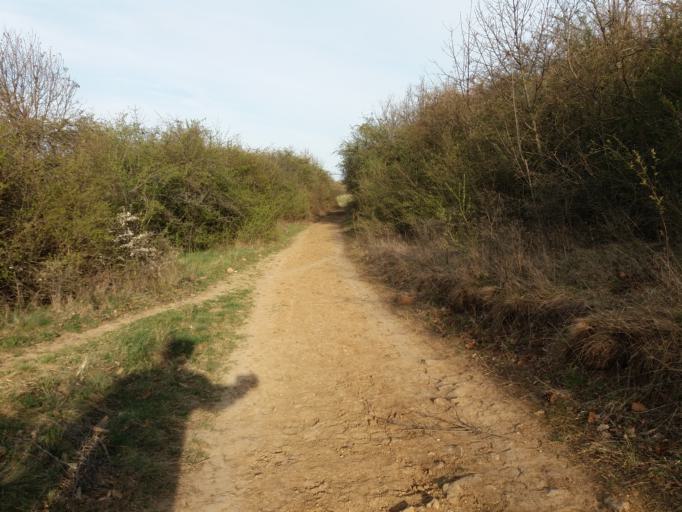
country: HU
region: Pest
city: Pilisborosjeno
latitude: 47.6227
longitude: 19.0120
